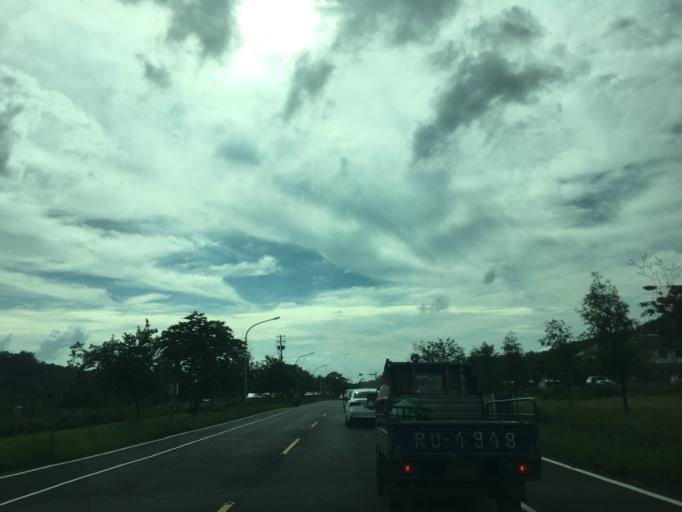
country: TW
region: Taiwan
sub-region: Chiayi
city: Jiayi Shi
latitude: 23.4464
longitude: 120.5822
